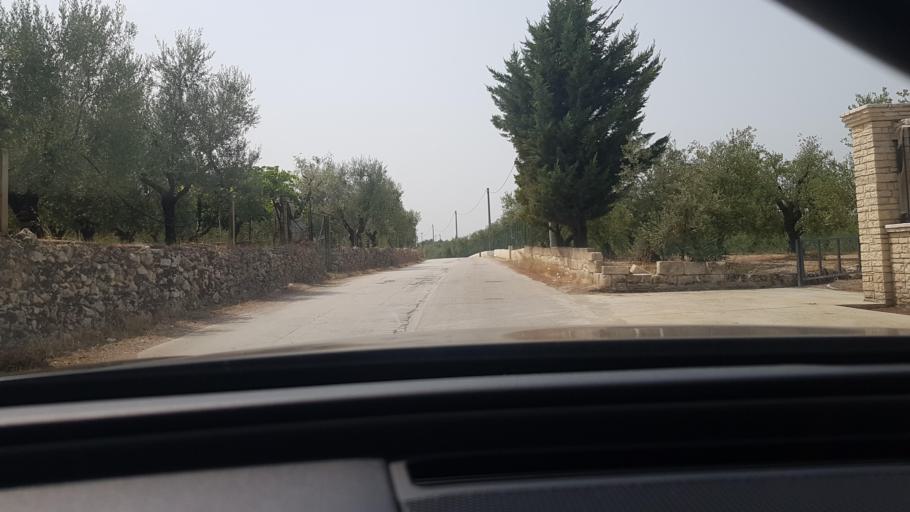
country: IT
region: Apulia
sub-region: Provincia di Barletta - Andria - Trani
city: Andria
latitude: 41.2238
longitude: 16.2664
